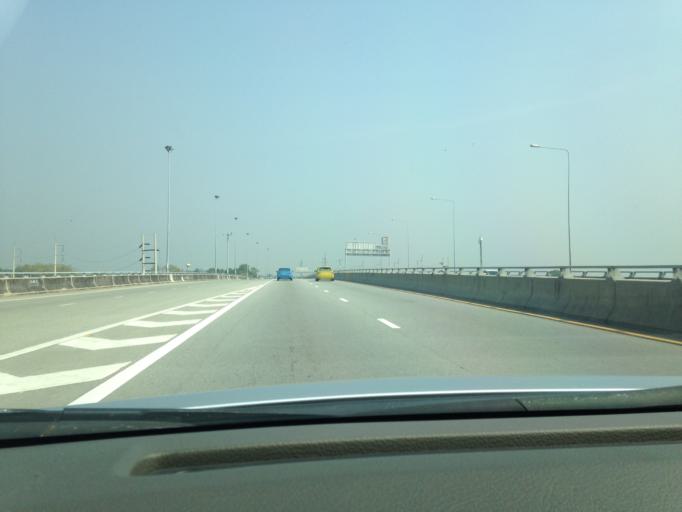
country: TH
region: Phra Nakhon Si Ayutthaya
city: Ban Bang Kadi Pathum Thani
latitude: 14.0067
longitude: 100.5713
